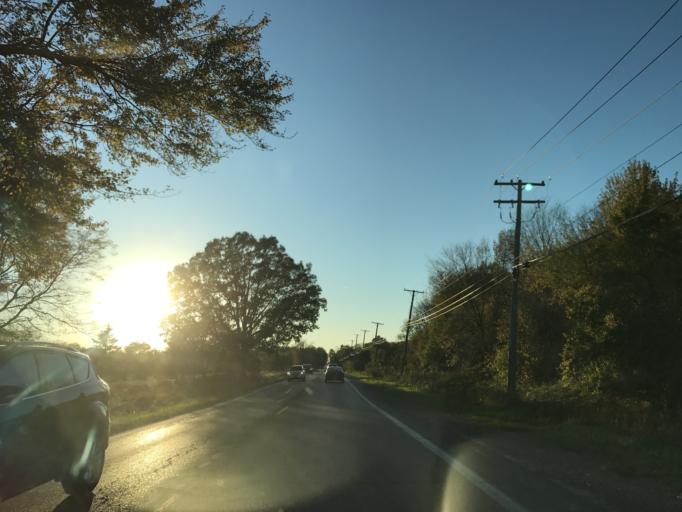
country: US
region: Michigan
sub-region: Oakland County
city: South Lyon
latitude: 42.4627
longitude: -83.5953
